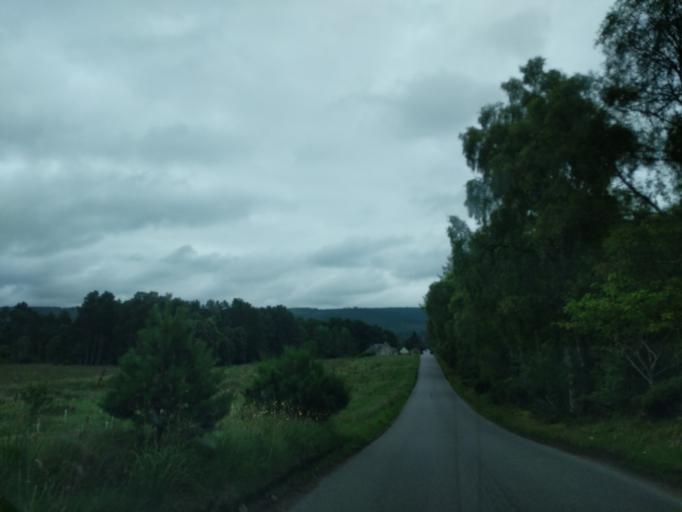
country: GB
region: Scotland
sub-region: Moray
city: Kinloss
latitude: 57.5492
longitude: -3.4751
